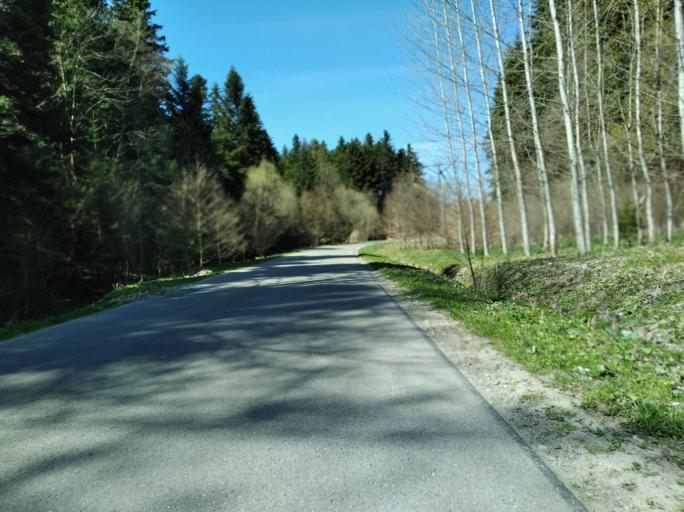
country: PL
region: Subcarpathian Voivodeship
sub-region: Powiat brzozowski
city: Golcowa
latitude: 49.7505
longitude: 22.0693
